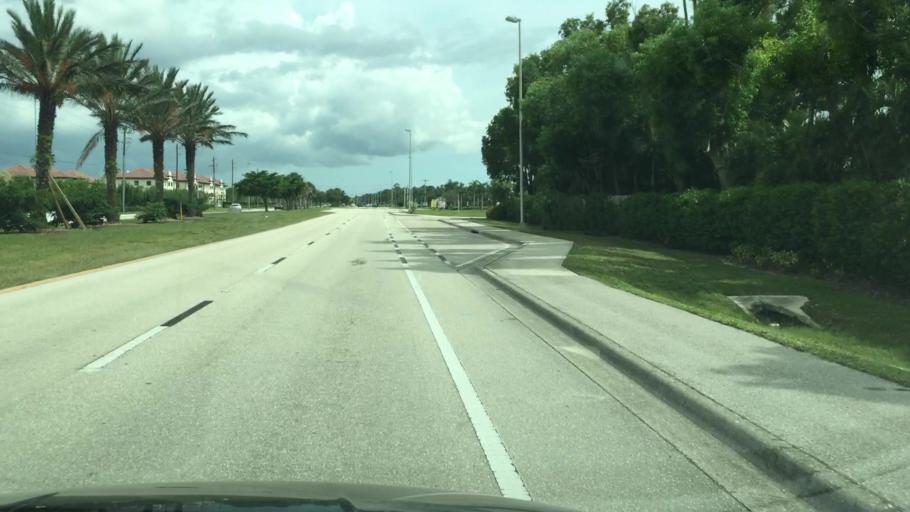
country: US
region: Florida
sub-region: Lee County
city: Three Oaks
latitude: 26.4538
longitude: -81.7889
